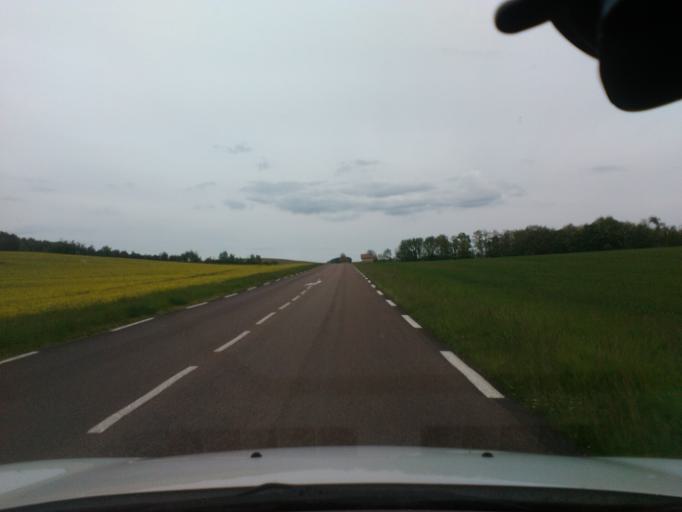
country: FR
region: Champagne-Ardenne
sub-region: Departement de l'Aube
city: Bar-sur-Aube
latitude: 48.2238
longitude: 4.7705
